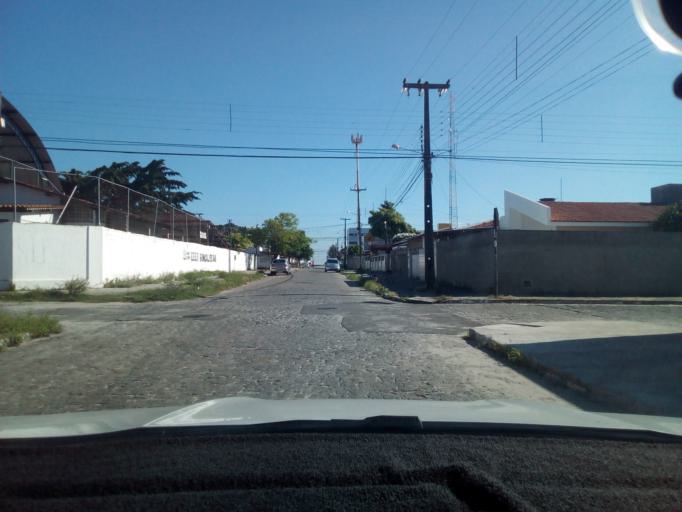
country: BR
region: Paraiba
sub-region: Joao Pessoa
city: Joao Pessoa
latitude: -7.1516
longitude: -34.8787
